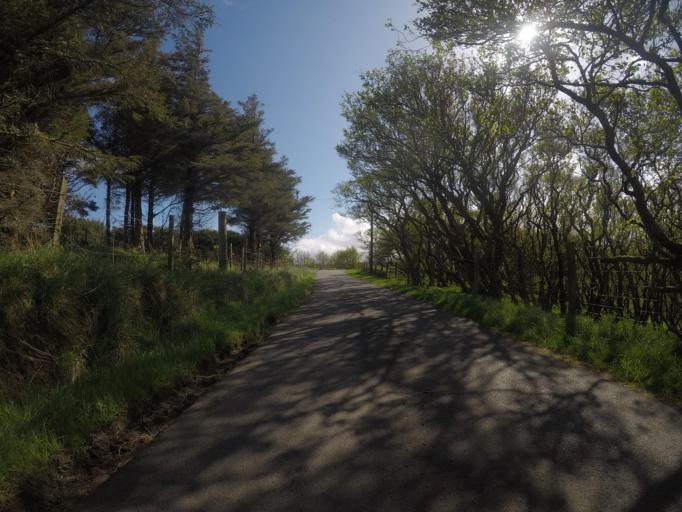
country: GB
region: Scotland
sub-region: Highland
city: Portree
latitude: 57.6318
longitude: -6.2178
